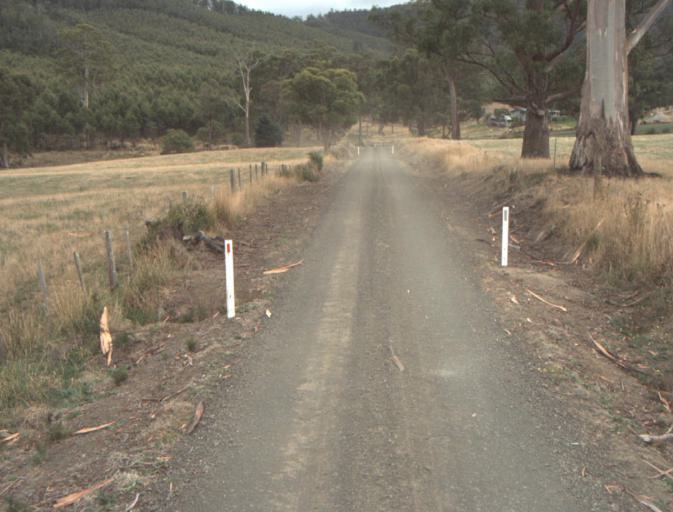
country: AU
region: Tasmania
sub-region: Dorset
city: Scottsdale
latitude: -41.4639
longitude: 147.5716
